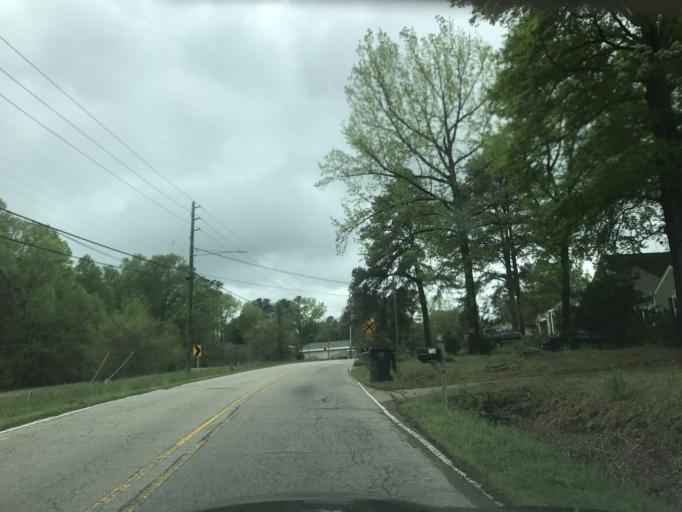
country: US
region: North Carolina
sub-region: Wake County
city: Raleigh
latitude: 35.7463
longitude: -78.6546
